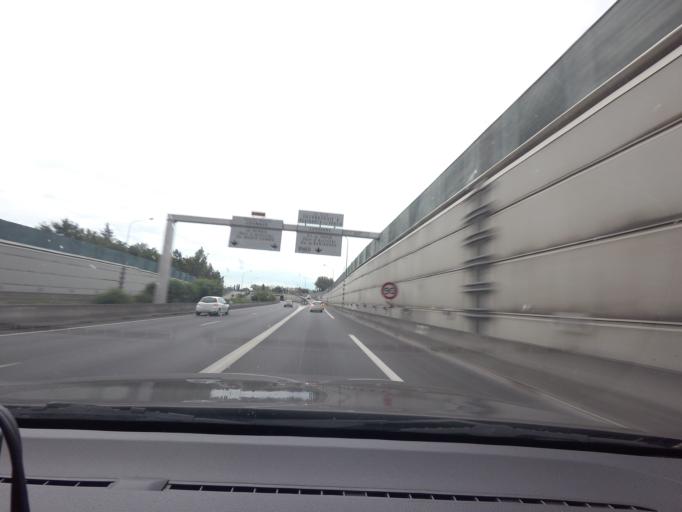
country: FR
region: Midi-Pyrenees
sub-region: Departement de la Haute-Garonne
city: Colomiers
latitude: 43.5913
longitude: 1.3608
